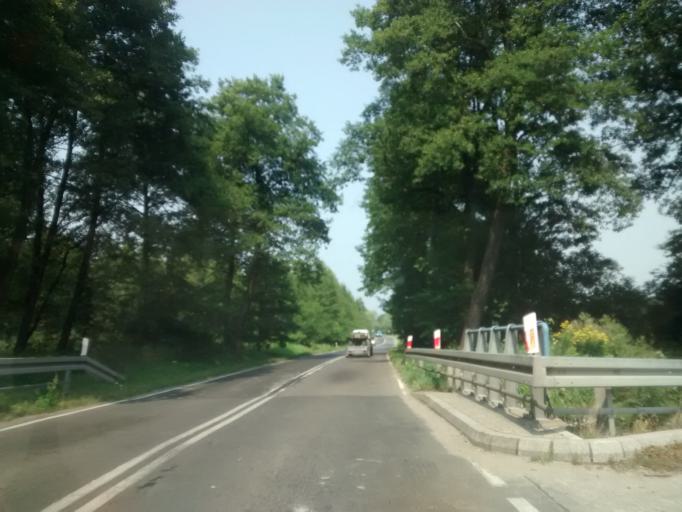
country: PL
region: Lesser Poland Voivodeship
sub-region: Powiat olkuski
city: Klucze
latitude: 50.3564
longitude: 19.5613
